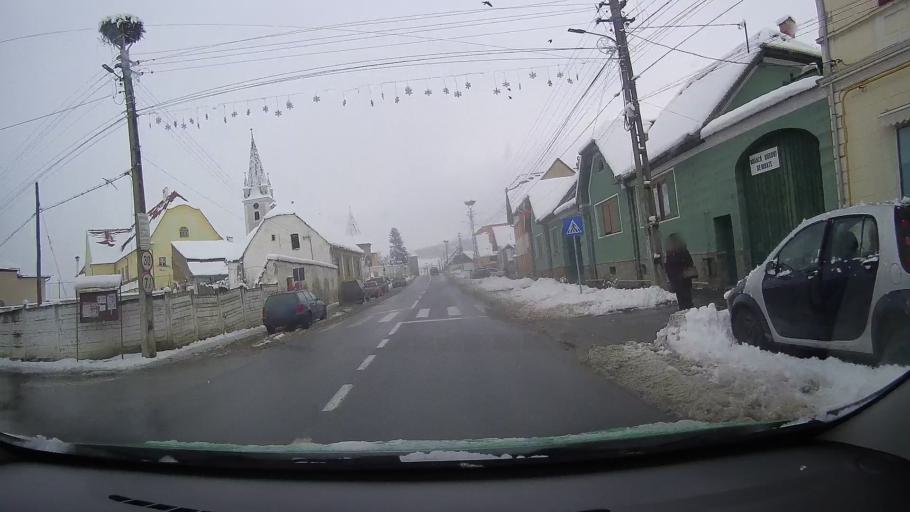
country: RO
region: Sibiu
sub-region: Comuna Cristian
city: Cristian
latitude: 45.7831
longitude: 24.0283
